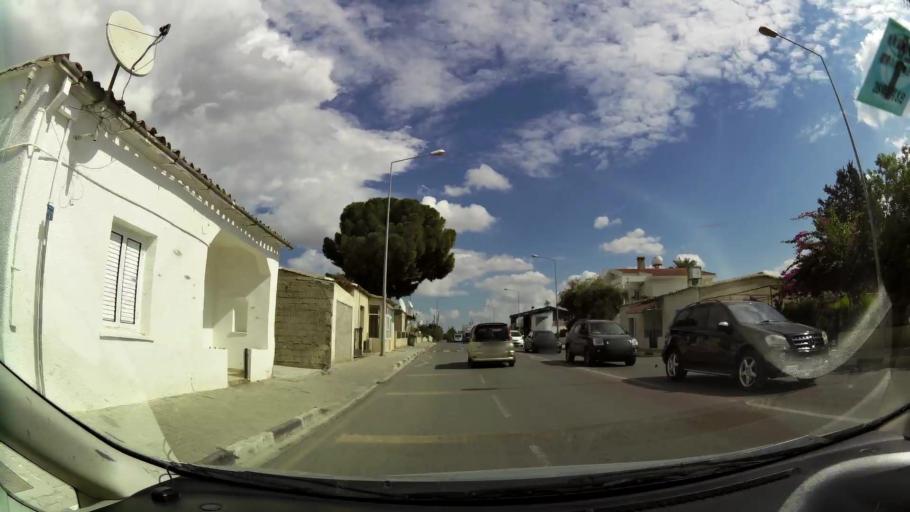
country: CY
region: Lefkosia
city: Nicosia
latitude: 35.1984
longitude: 33.3551
